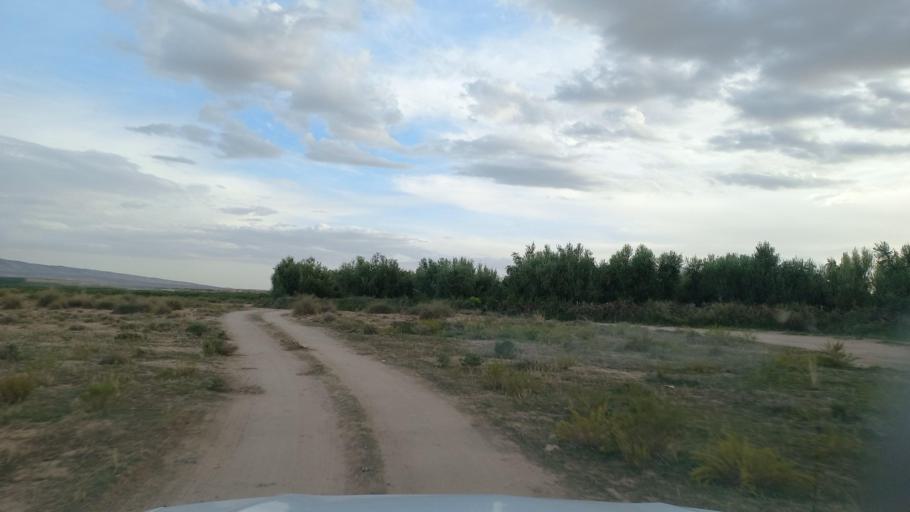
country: TN
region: Al Qasrayn
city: Sbiba
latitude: 35.4292
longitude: 9.0981
